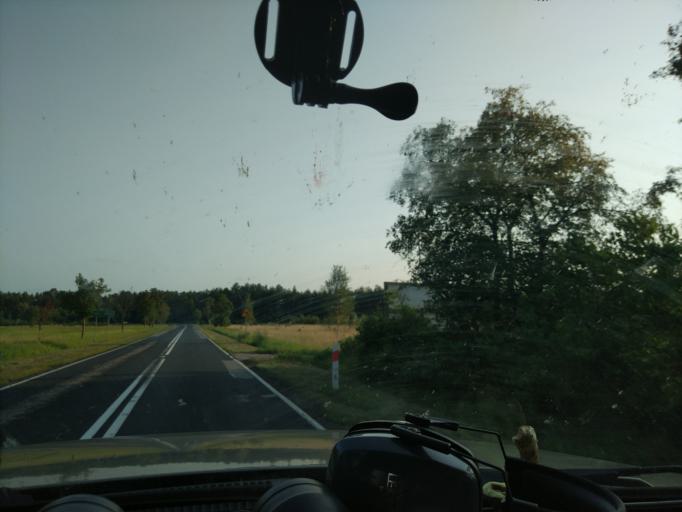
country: PL
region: Warmian-Masurian Voivodeship
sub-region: Powiat szczycienski
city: Wielbark
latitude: 53.3479
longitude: 20.9001
